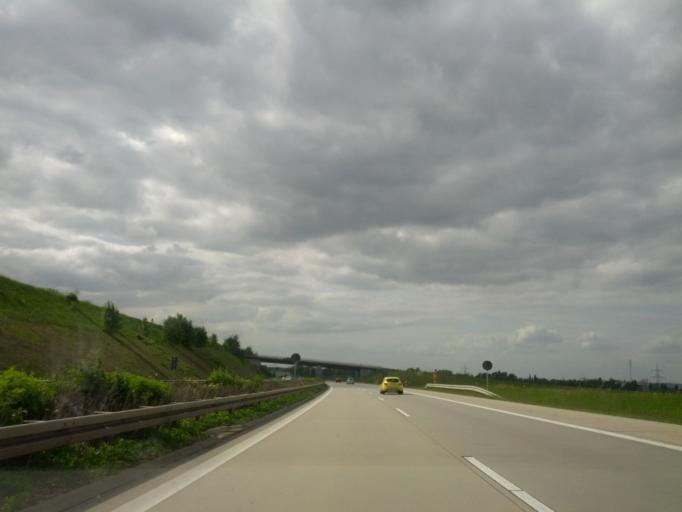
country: DE
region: Saxony
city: Bannewitz
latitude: 50.9936
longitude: 13.7665
